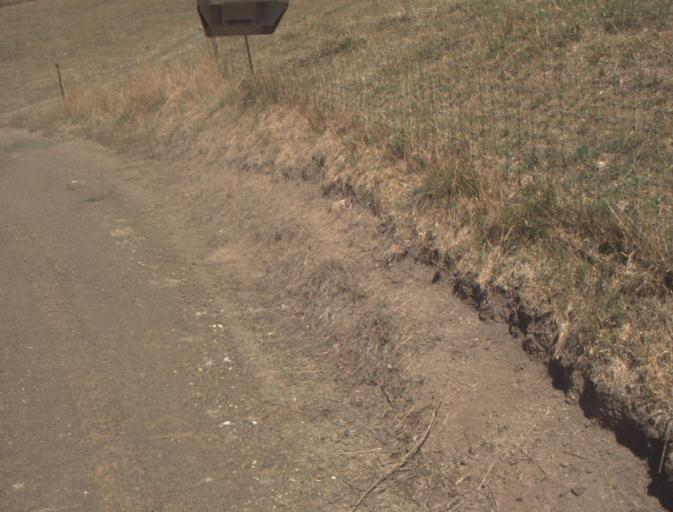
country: AU
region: Tasmania
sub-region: Launceston
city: Mayfield
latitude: -41.2657
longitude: 147.1285
